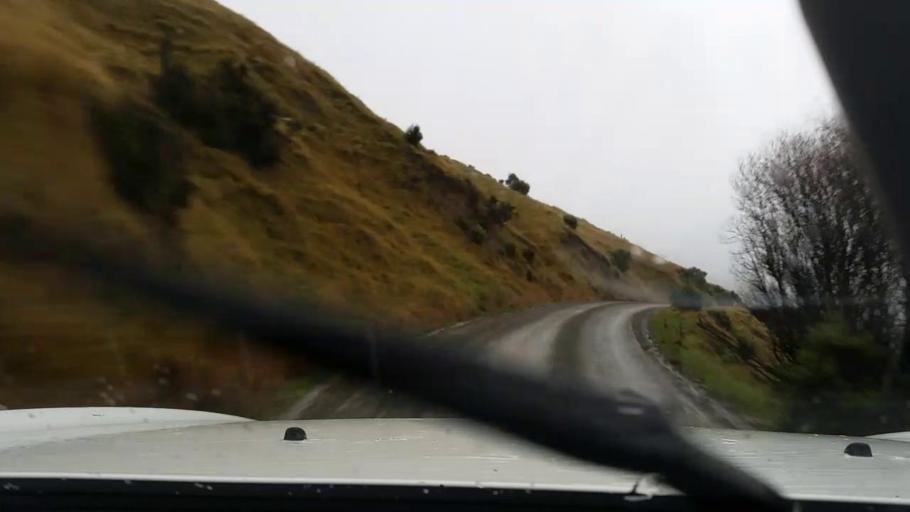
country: NZ
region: Wellington
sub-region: Masterton District
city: Masterton
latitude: -41.2502
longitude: 175.8891
